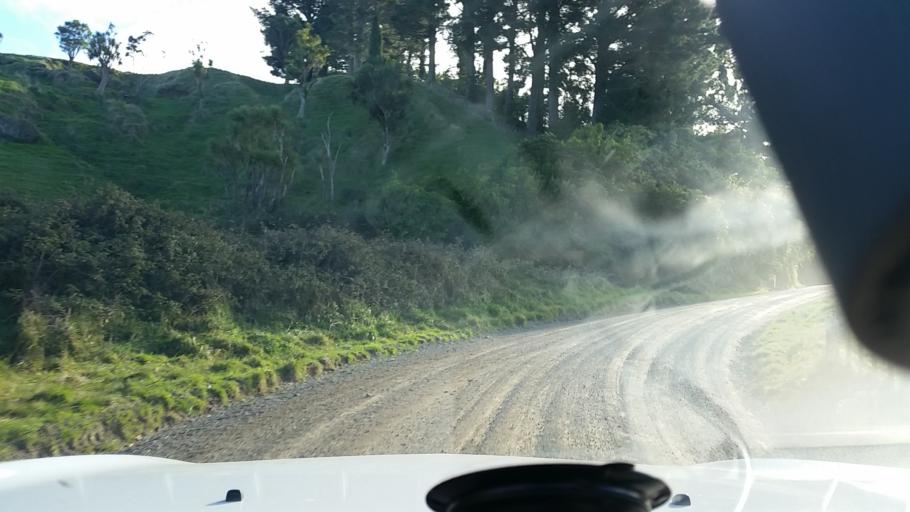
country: NZ
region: Hawke's Bay
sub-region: Napier City
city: Napier
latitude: -39.2638
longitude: 176.8508
